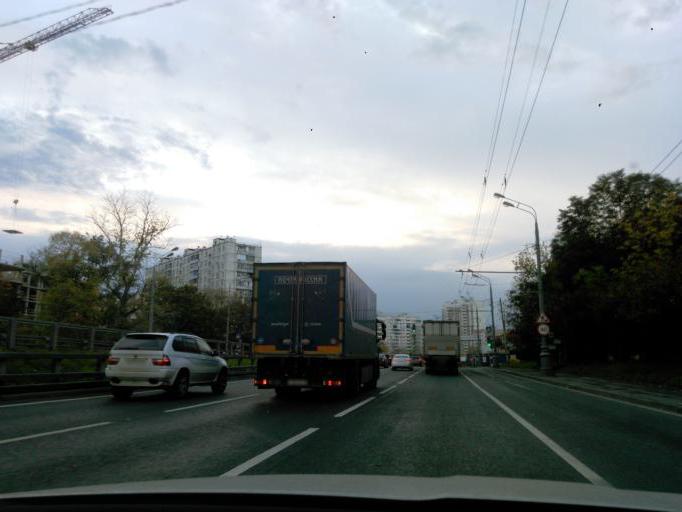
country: RU
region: Moscow
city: Likhobory
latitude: 55.8587
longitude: 37.5575
